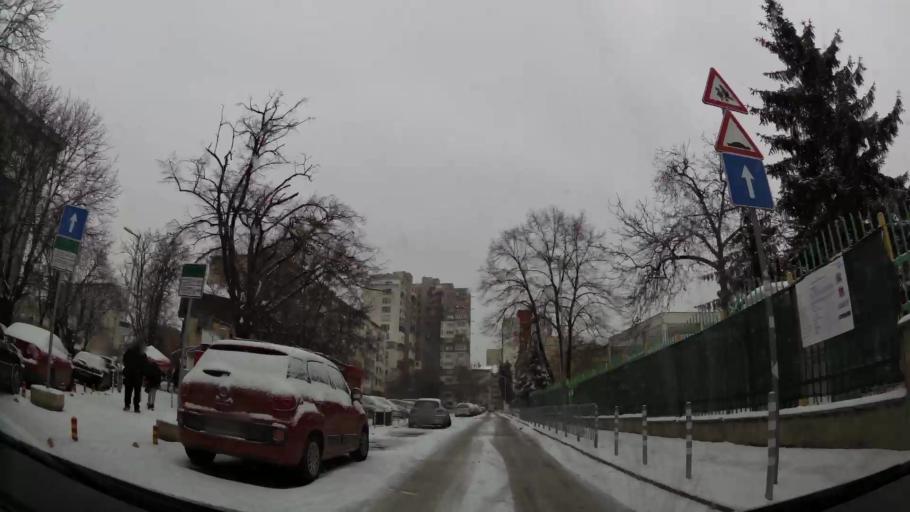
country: BG
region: Sofia-Capital
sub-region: Stolichna Obshtina
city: Sofia
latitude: 42.6856
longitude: 23.3033
